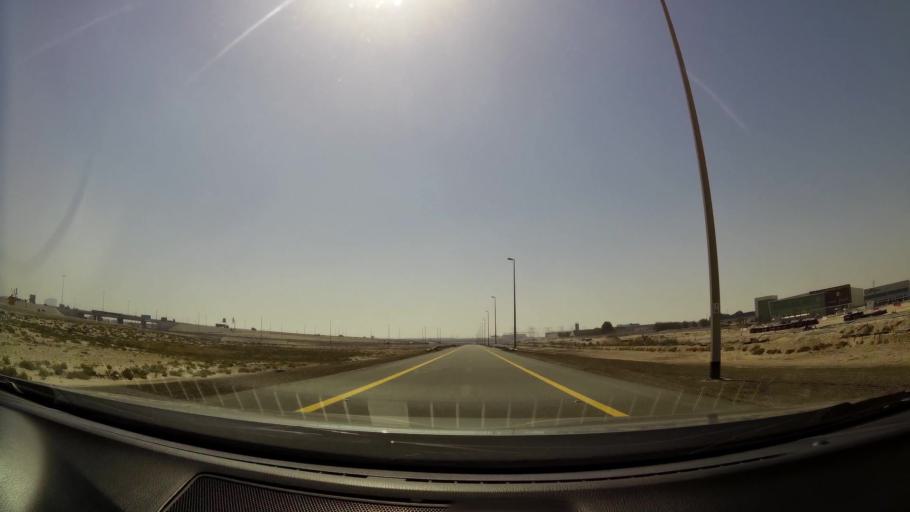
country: AE
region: Dubai
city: Dubai
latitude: 24.9446
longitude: 55.0586
